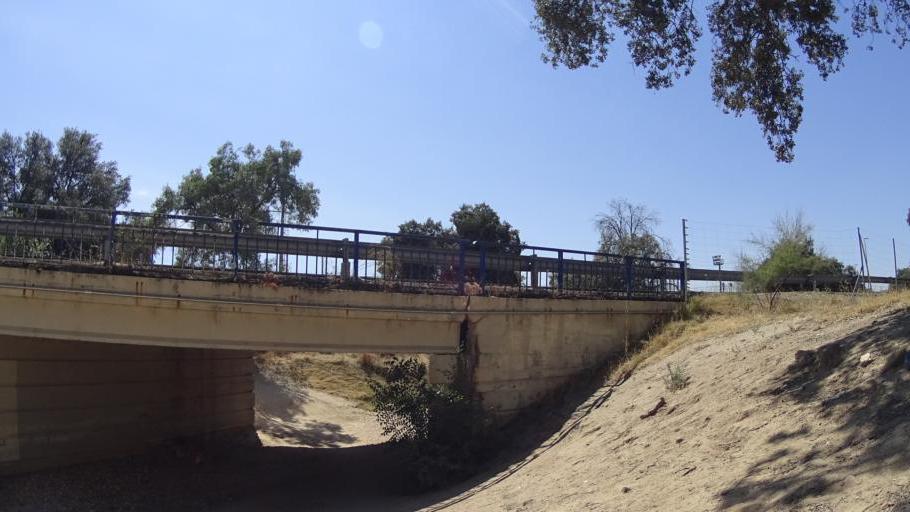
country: ES
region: Madrid
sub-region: Provincia de Madrid
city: Boadilla del Monte
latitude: 40.4182
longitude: -3.8589
